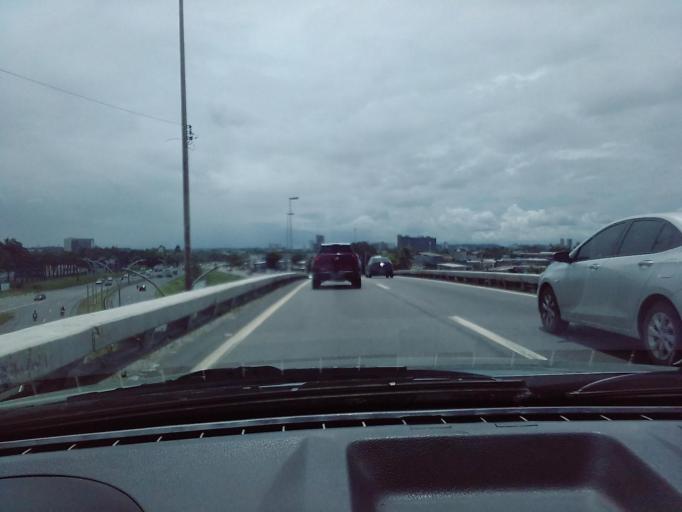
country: BR
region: Pernambuco
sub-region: Recife
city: Recife
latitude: -8.0645
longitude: -34.9445
